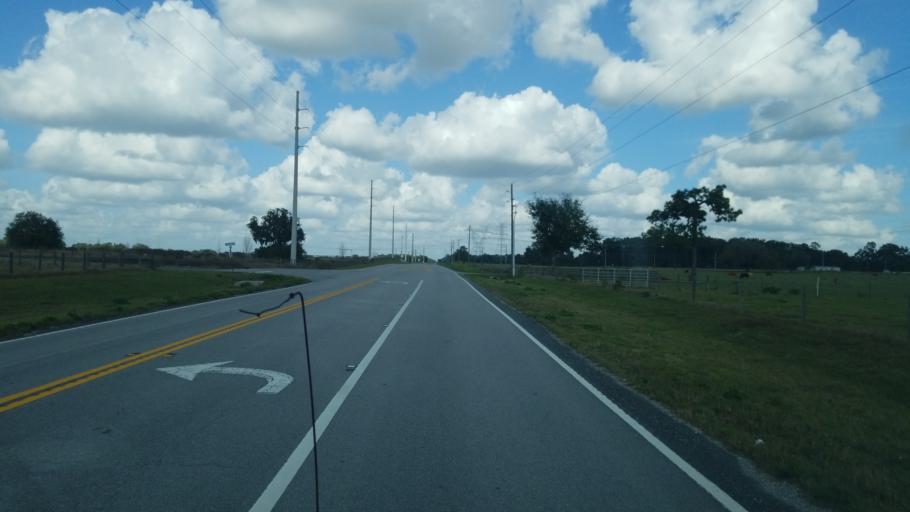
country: US
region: Florida
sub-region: Sumter County
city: Wildwood
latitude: 28.8900
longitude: -82.1200
